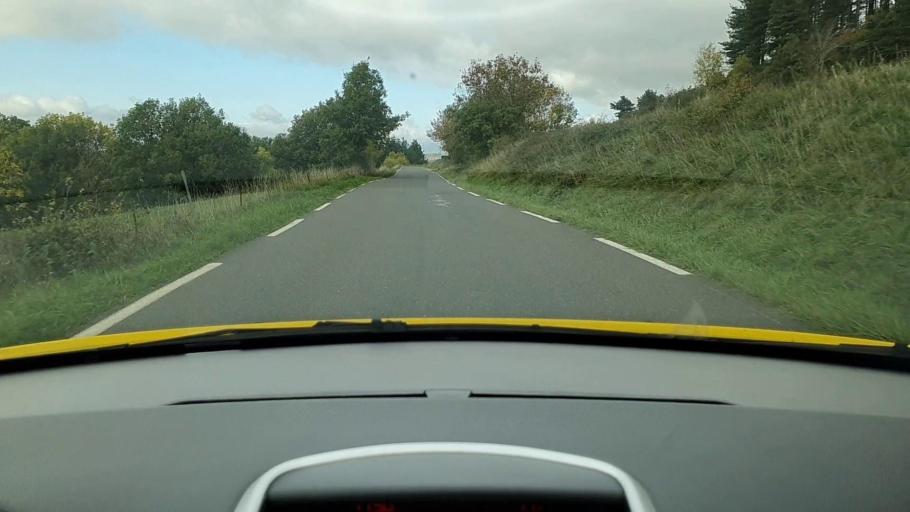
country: FR
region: Languedoc-Roussillon
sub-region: Departement de la Lozere
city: Meyrueis
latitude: 44.1285
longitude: 3.4055
